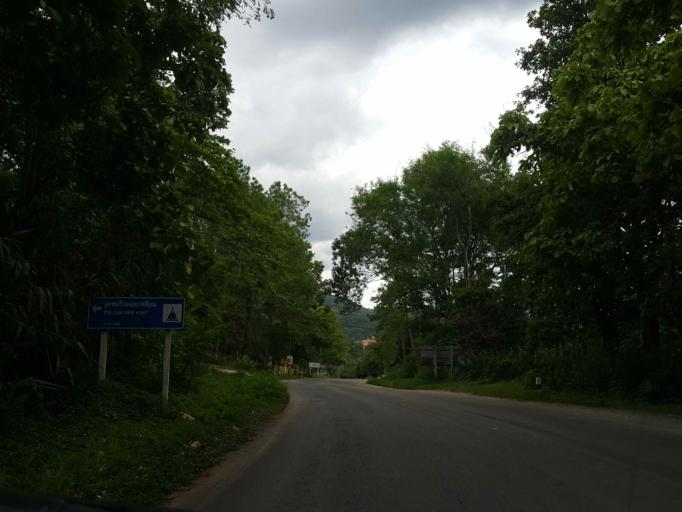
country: TH
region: Chiang Mai
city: Hang Dong
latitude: 18.7831
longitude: 98.8473
